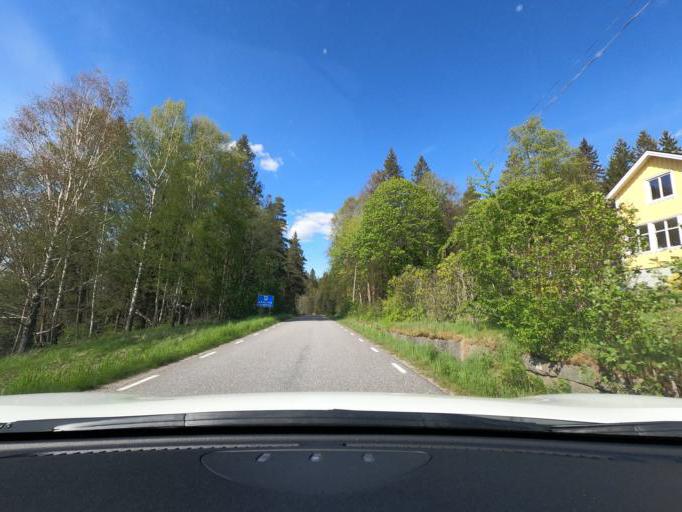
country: SE
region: Vaestra Goetaland
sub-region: Harryda Kommun
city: Ravlanda
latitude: 57.6148
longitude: 12.4951
